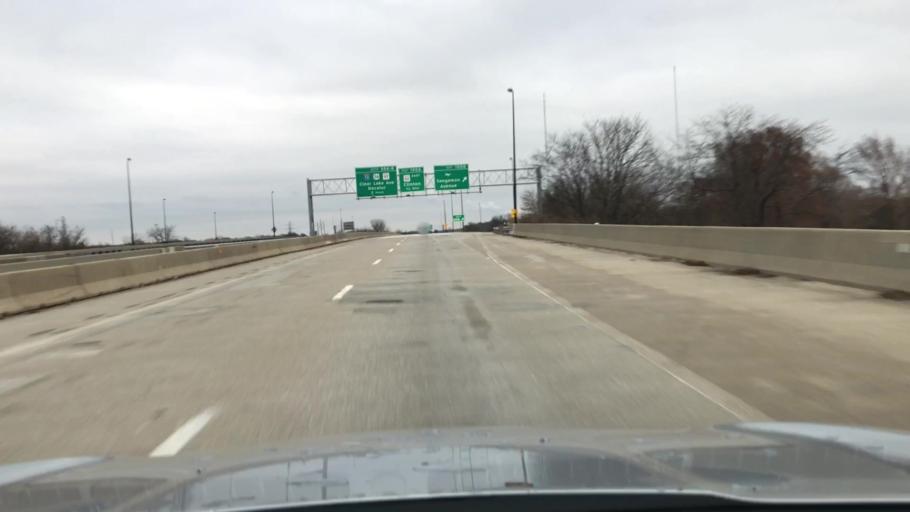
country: US
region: Illinois
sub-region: Sangamon County
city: Grandview
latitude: 39.8356
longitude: -89.5937
